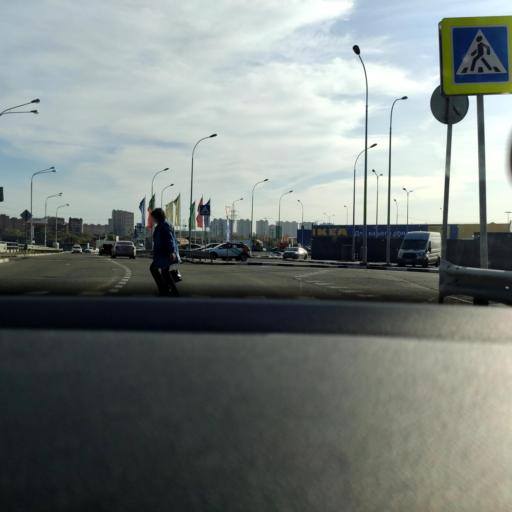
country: RU
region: Moskovskaya
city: Kotel'niki
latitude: 55.6572
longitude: 37.8489
